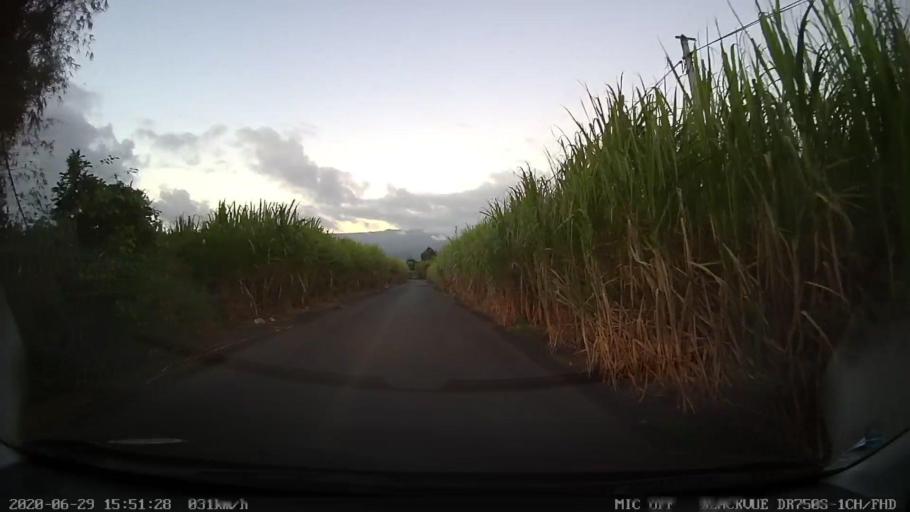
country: RE
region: Reunion
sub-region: Reunion
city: Bras-Panon
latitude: -20.9942
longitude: 55.6937
